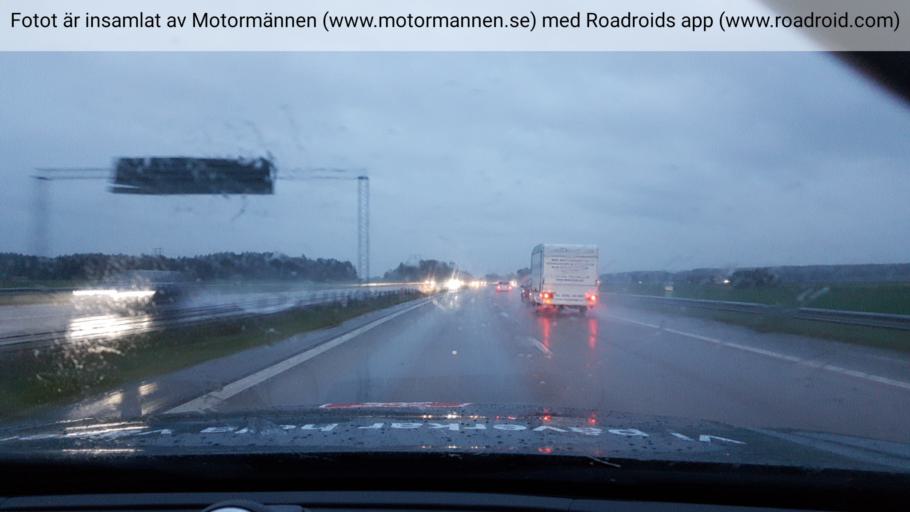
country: SE
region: Uppsala
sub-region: Uppsala Kommun
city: Saevja
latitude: 59.8248
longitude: 17.7451
